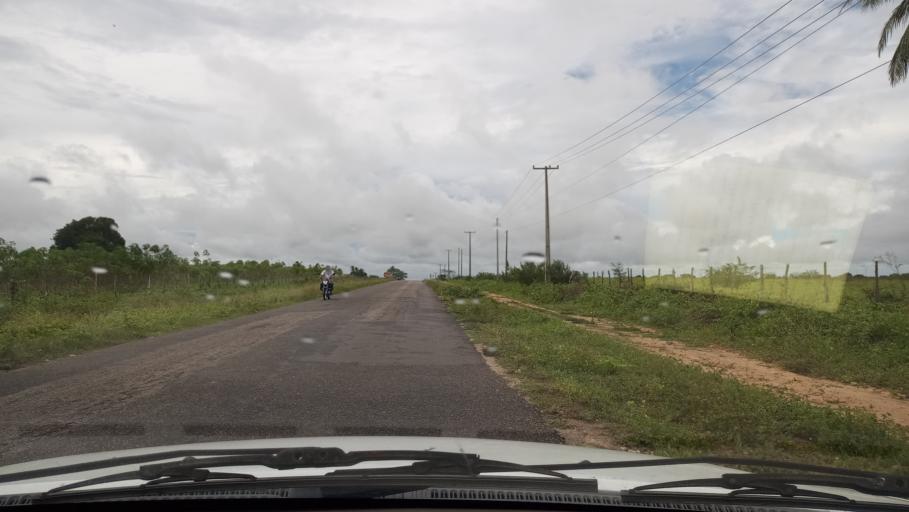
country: BR
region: Rio Grande do Norte
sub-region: Poco Branco
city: Poco Branco
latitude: -5.6163
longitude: -35.6514
